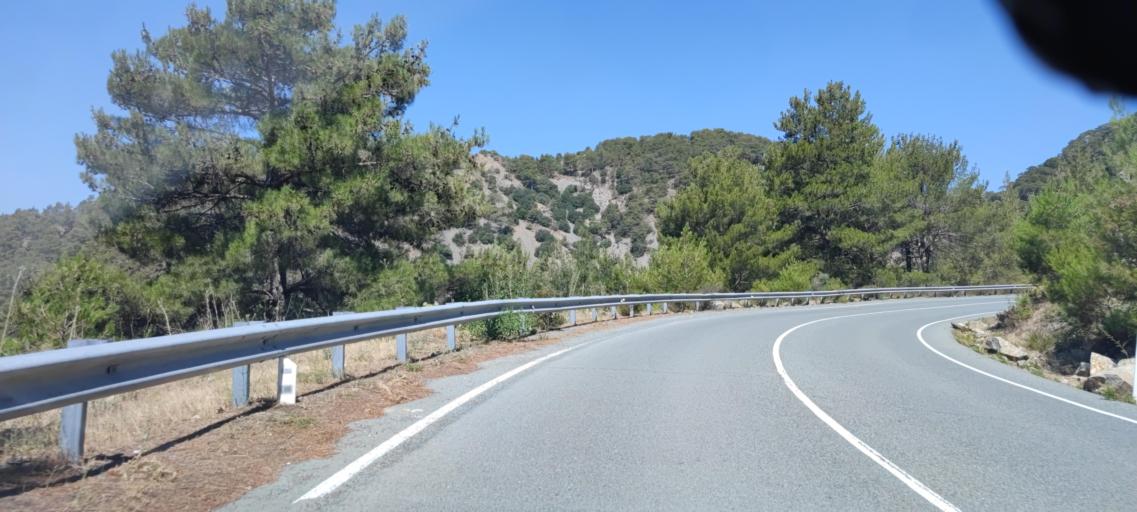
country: CY
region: Lefkosia
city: Kakopetria
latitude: 34.9050
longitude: 32.8137
